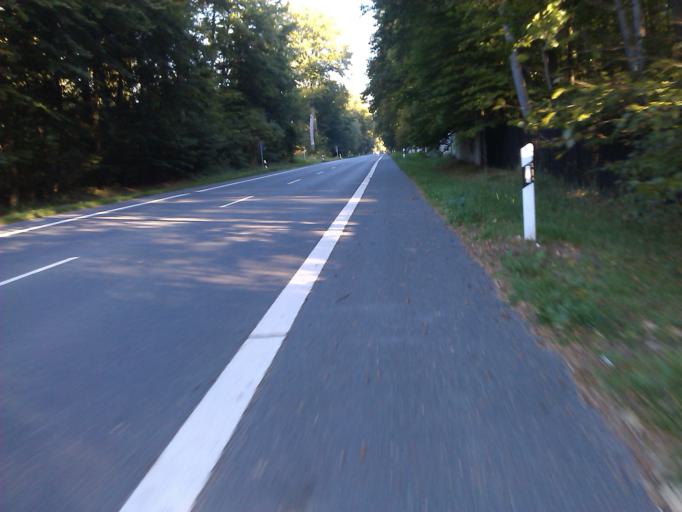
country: DE
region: Hesse
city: Langen
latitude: 49.9847
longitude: 8.6414
